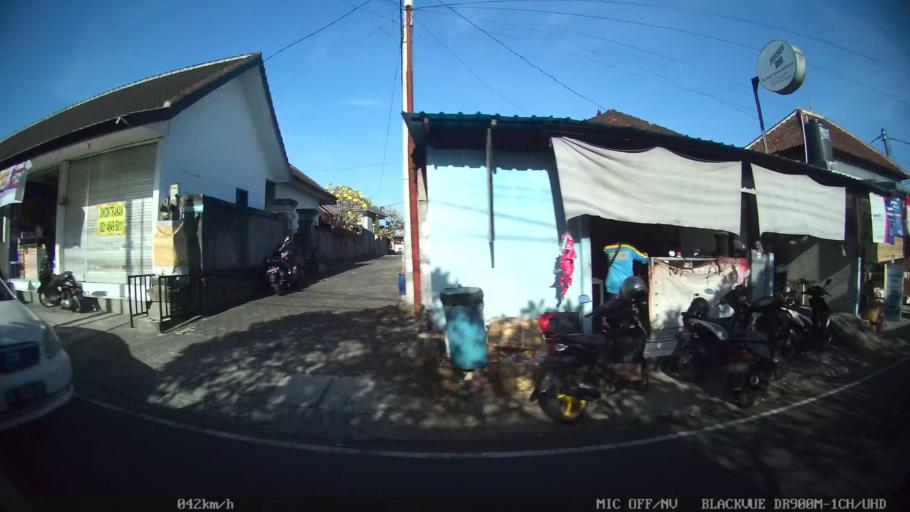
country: ID
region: Bali
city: Banjar Gunungpande
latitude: -8.6171
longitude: 115.1691
